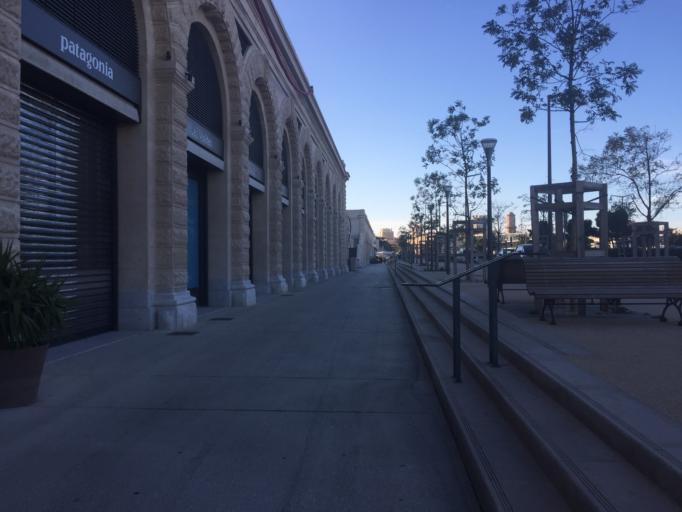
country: FR
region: Provence-Alpes-Cote d'Azur
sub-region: Departement des Bouches-du-Rhone
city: Marseille 02
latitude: 43.3008
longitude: 5.3643
